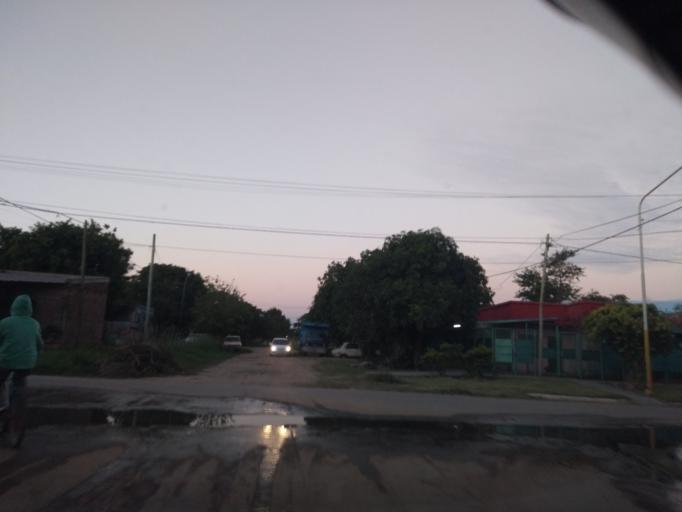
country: AR
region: Chaco
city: Barranqueras
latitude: -27.4837
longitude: -58.9335
